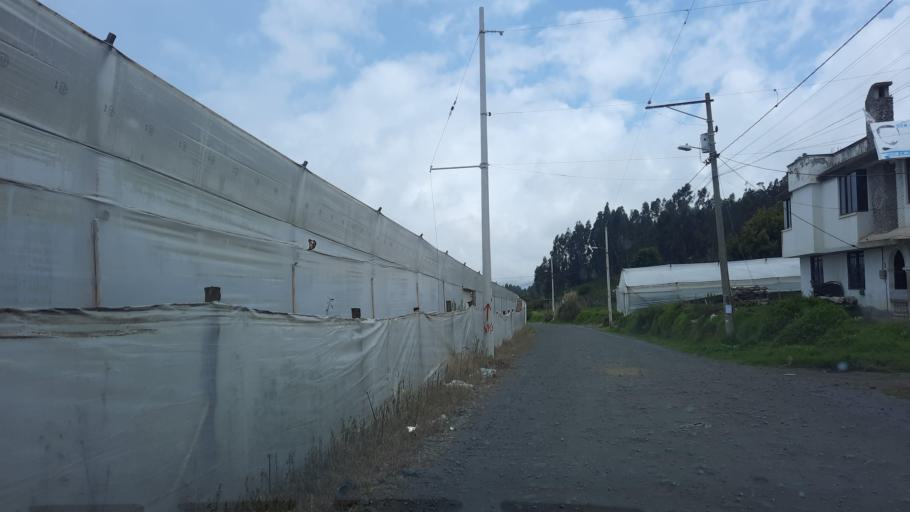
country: EC
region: Chimborazo
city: Riobamba
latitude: -1.6904
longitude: -78.6707
